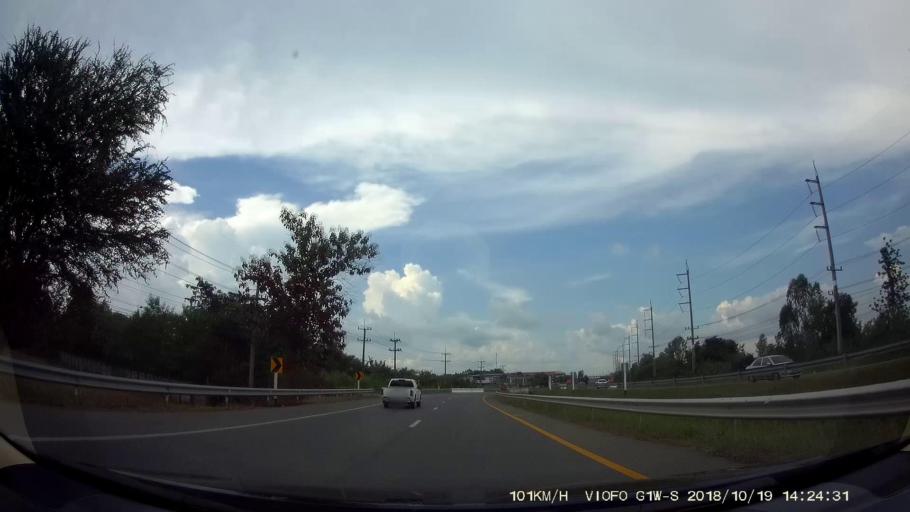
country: TH
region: Chaiyaphum
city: Kaeng Khro
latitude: 16.0817
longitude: 102.2717
